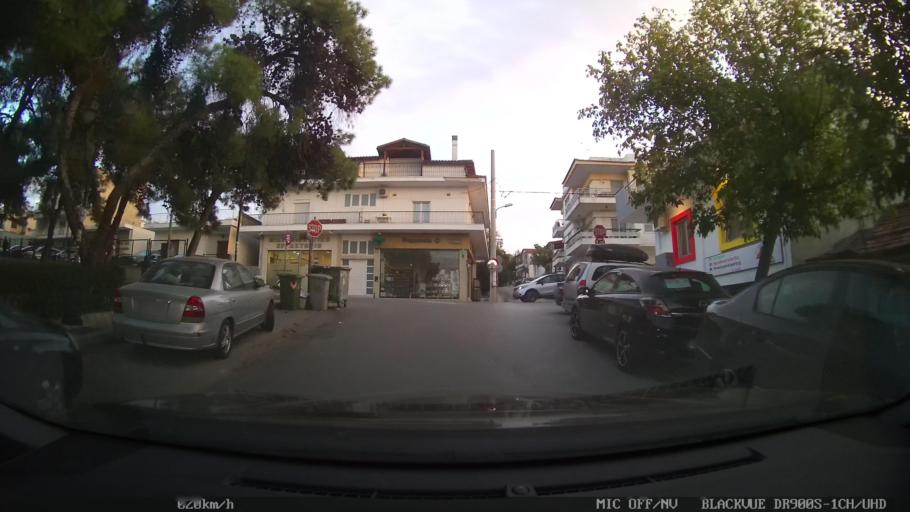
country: GR
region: Central Macedonia
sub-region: Nomos Thessalonikis
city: Pylaia
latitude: 40.5991
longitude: 22.9870
